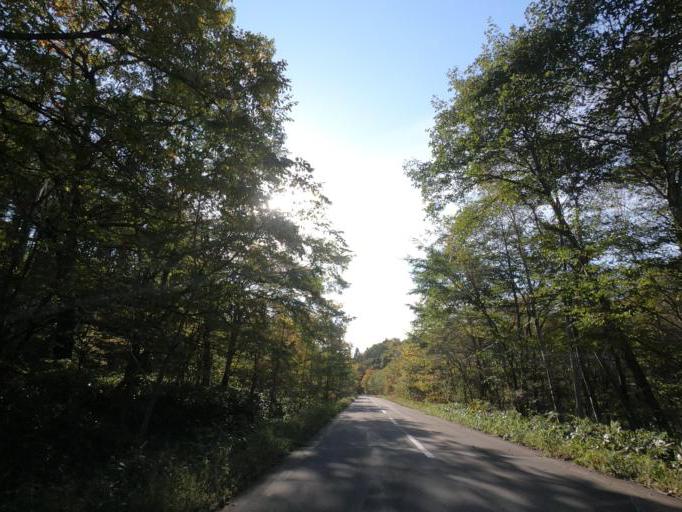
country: JP
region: Hokkaido
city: Obihiro
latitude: 42.6011
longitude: 143.3820
